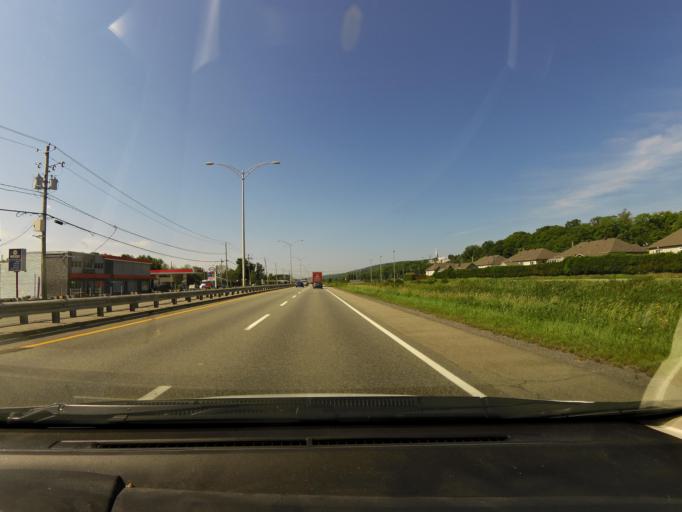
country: CA
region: Quebec
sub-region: Capitale-Nationale
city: Chateau-Richer
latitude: 46.9177
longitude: -71.0831
